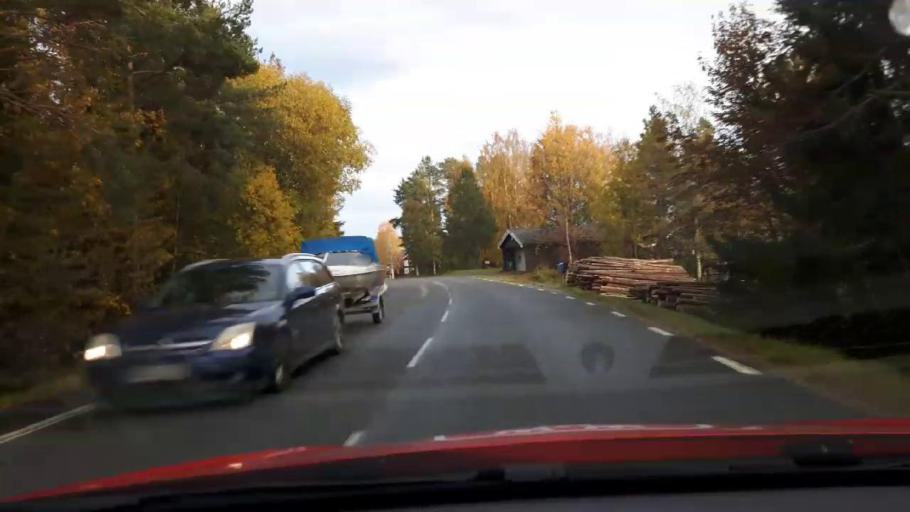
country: SE
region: Jaemtland
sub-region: Krokoms Kommun
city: Krokom
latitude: 63.3457
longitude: 14.5647
